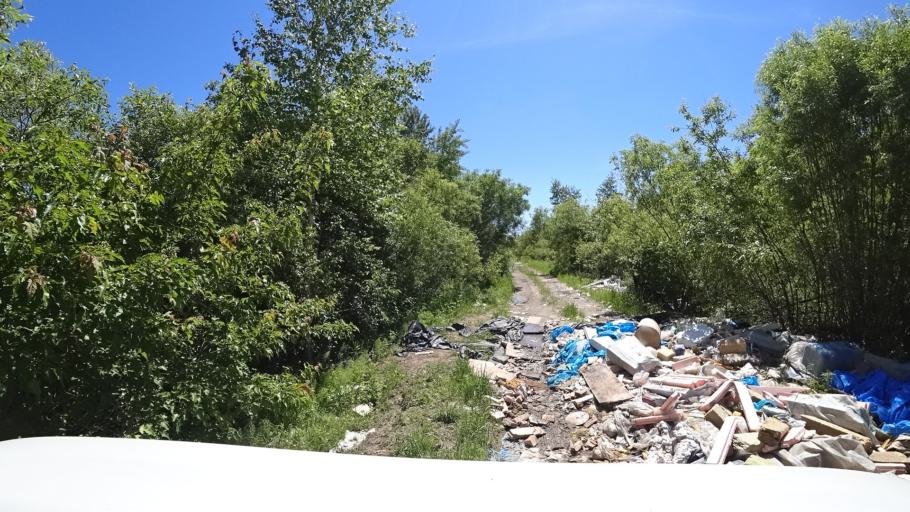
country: RU
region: Khabarovsk Krai
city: Topolevo
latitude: 48.4875
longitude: 135.1771
